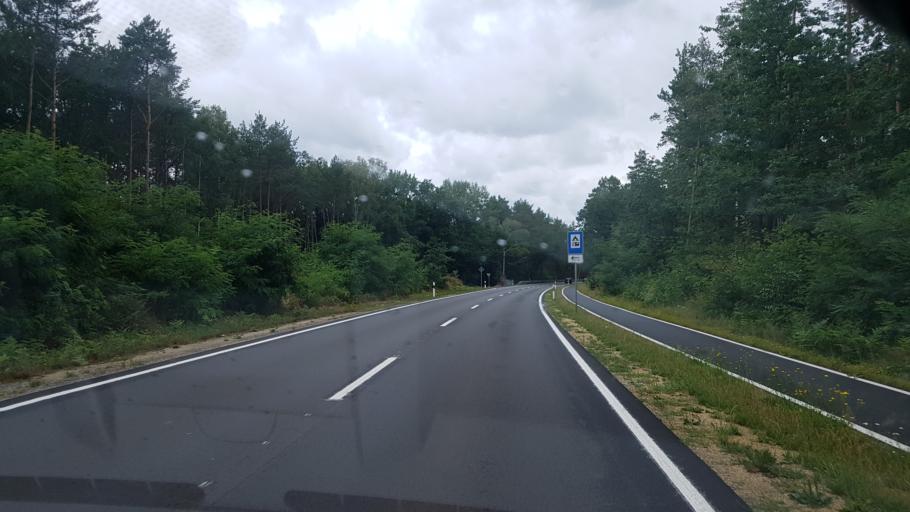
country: DE
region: Saxony
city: Niesky
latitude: 51.2976
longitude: 14.8088
